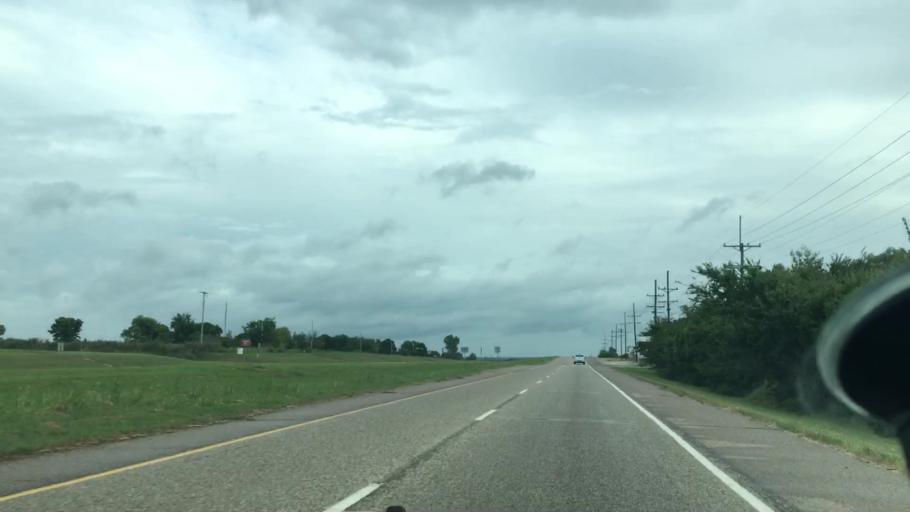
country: US
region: Oklahoma
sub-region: Seminole County
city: Seminole
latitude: 35.2916
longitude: -96.6713
